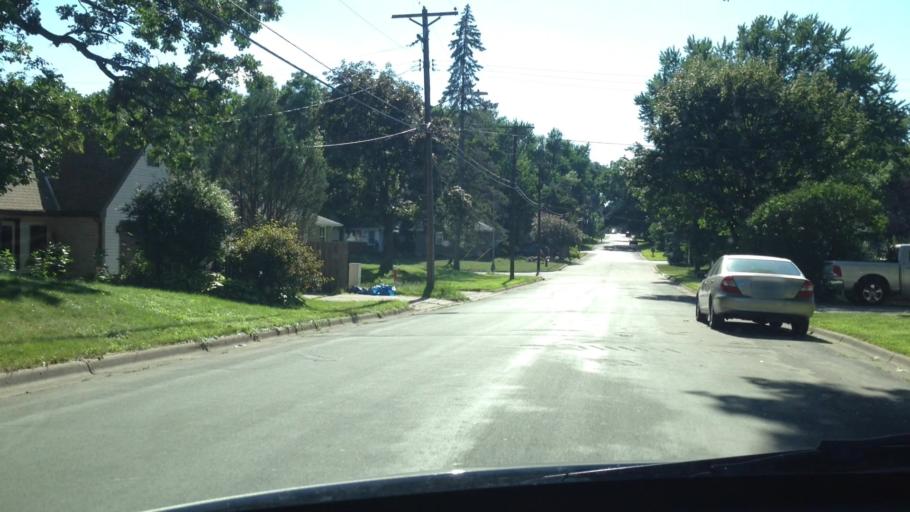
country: US
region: Minnesota
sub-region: Hennepin County
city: Richfield
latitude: 44.8799
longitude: -93.2999
